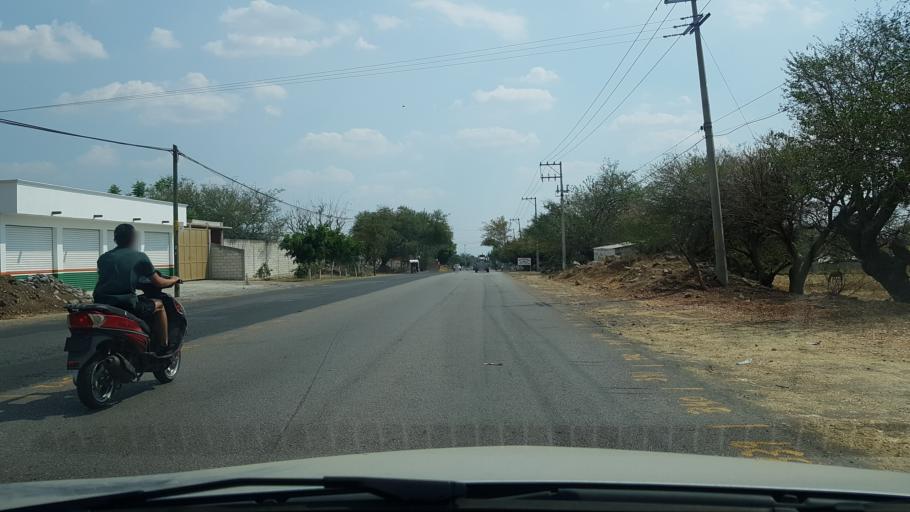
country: MX
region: Morelos
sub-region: Temoac
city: Huazulco
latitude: 18.7506
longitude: -98.7818
